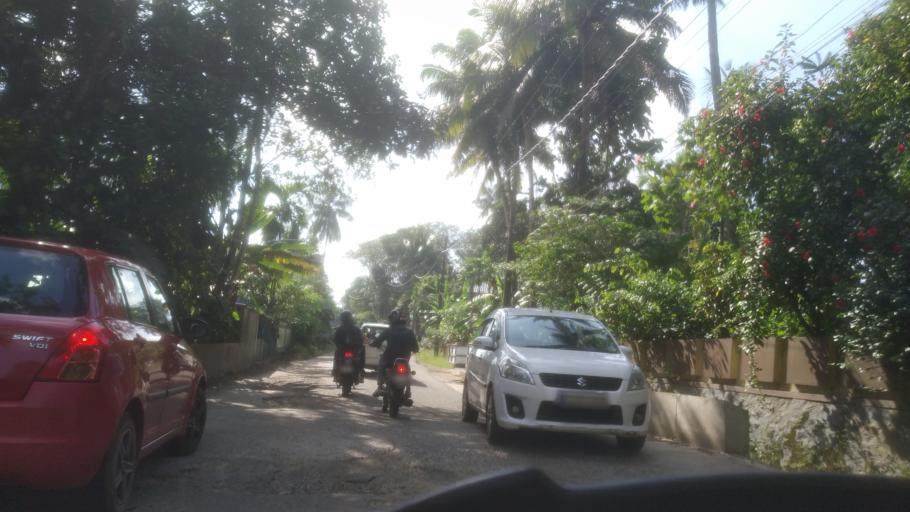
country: IN
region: Kerala
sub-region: Ernakulam
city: Muvattupula
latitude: 9.9982
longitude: 76.6241
